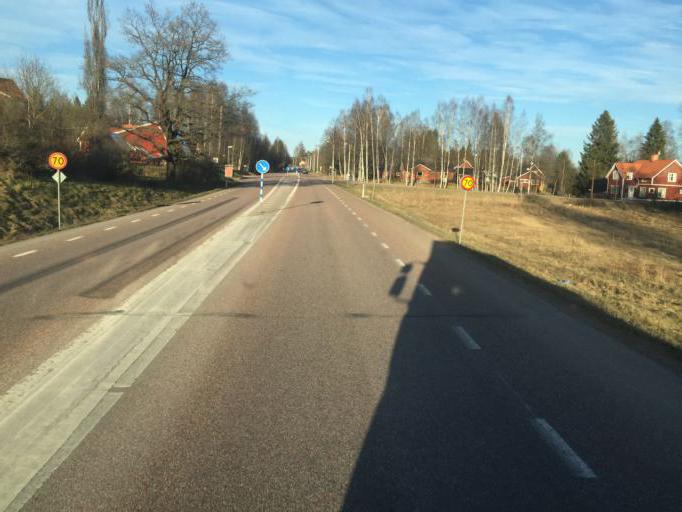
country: SE
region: Dalarna
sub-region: Gagnefs Kommun
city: Djuras
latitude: 60.5506
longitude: 15.1808
